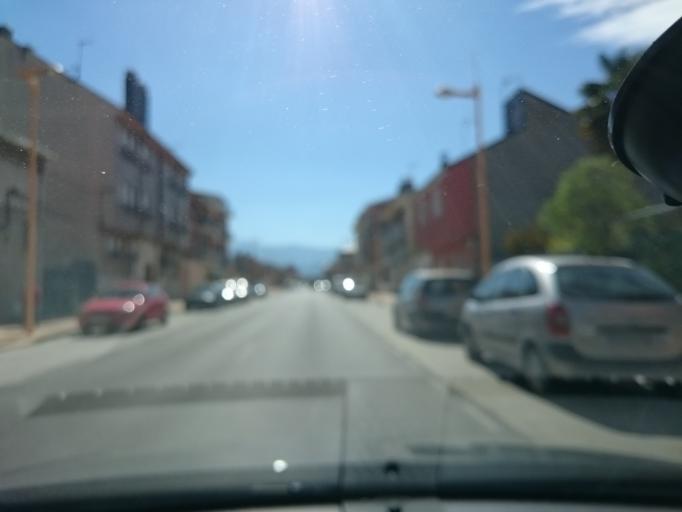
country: ES
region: Castille and Leon
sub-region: Provincia de Leon
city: Camponaraya
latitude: 42.5710
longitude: -6.6397
